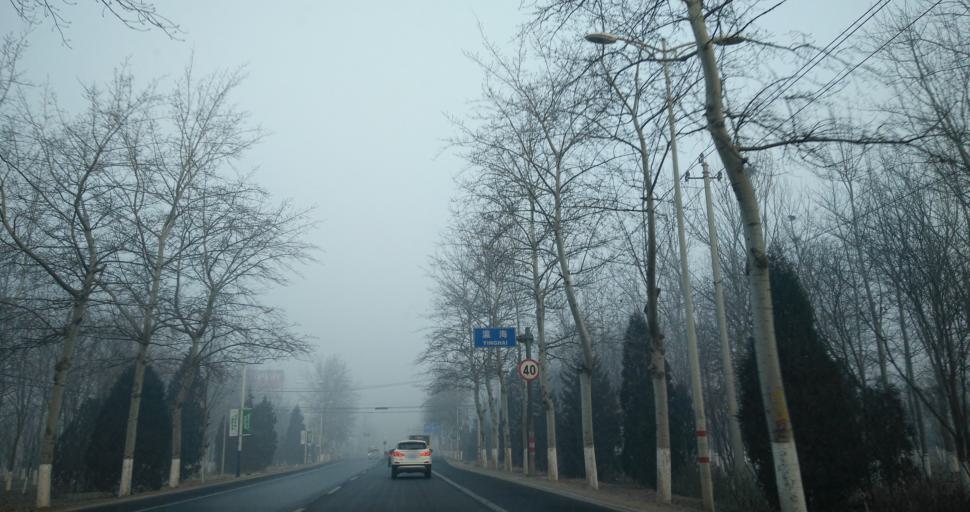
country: CN
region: Beijing
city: Yinghai
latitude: 39.7525
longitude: 116.4456
